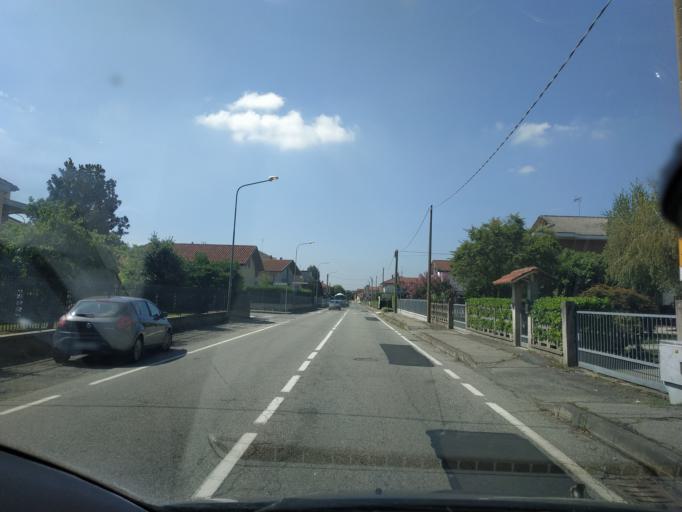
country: IT
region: Piedmont
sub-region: Provincia di Torino
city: San Benigno Canavese
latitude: 45.2295
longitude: 7.7887
